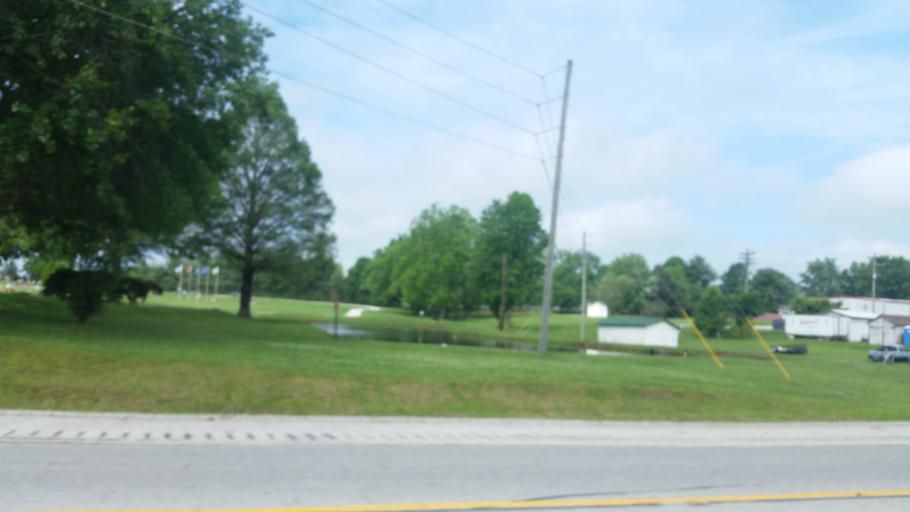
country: US
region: Kentucky
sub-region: Rowan County
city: Morehead
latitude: 38.2074
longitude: -83.4741
